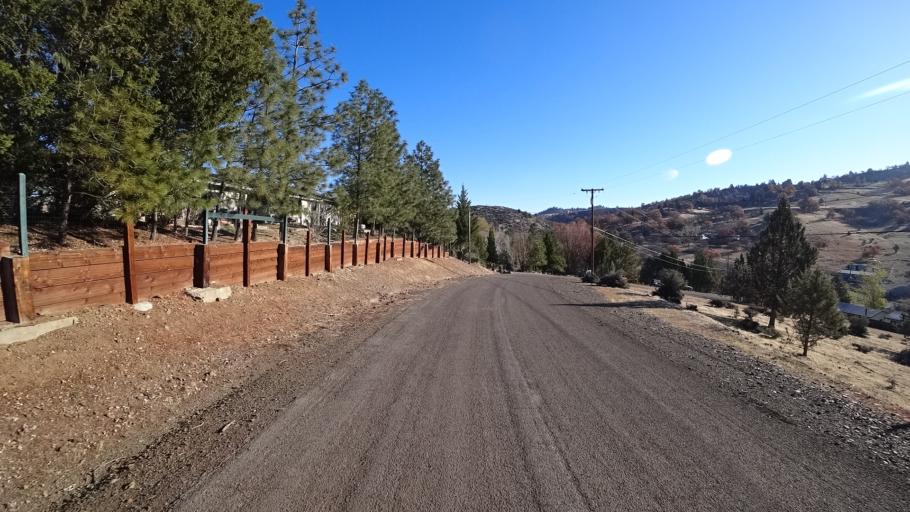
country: US
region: California
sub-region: Siskiyou County
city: Montague
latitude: 41.8948
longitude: -122.4801
